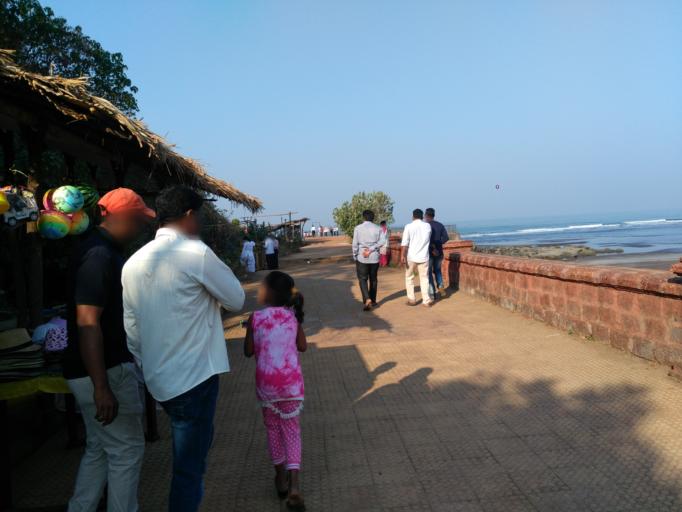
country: IN
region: Maharashtra
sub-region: Raigarh
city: Srivardhan
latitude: 17.9926
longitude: 73.0206
